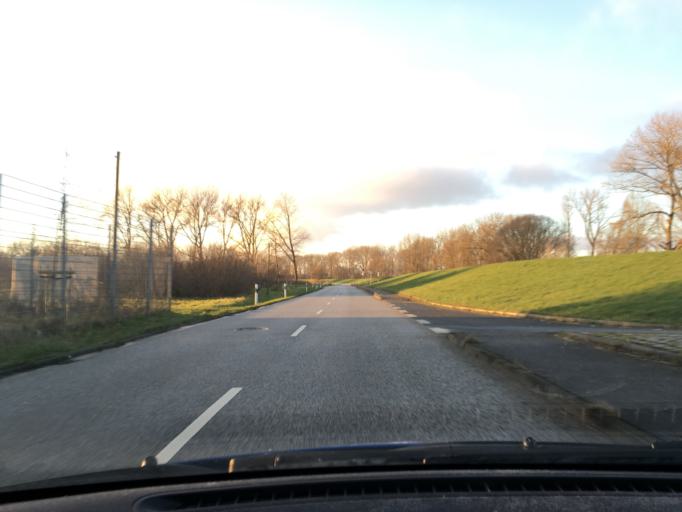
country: DE
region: Hamburg
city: Harburg
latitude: 53.4699
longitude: 10.0362
